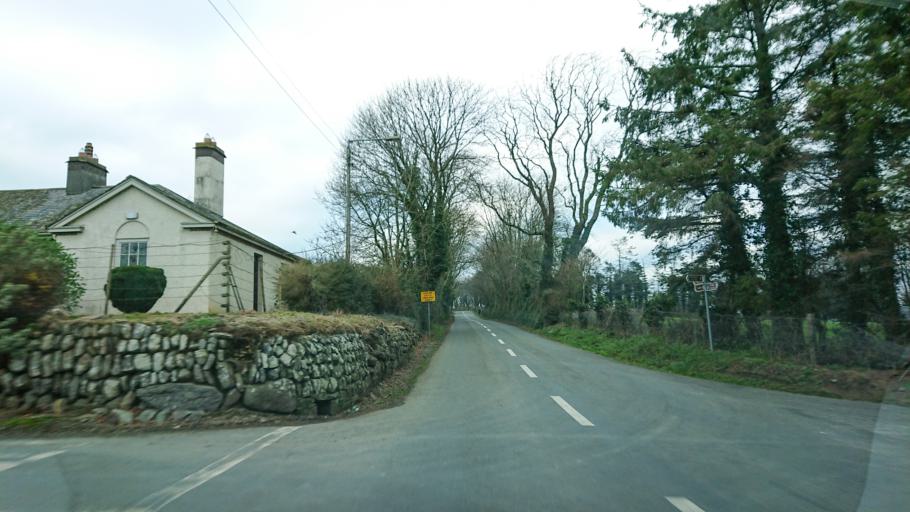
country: IE
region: Munster
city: Carrick-on-Suir
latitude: 52.3075
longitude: -7.5033
